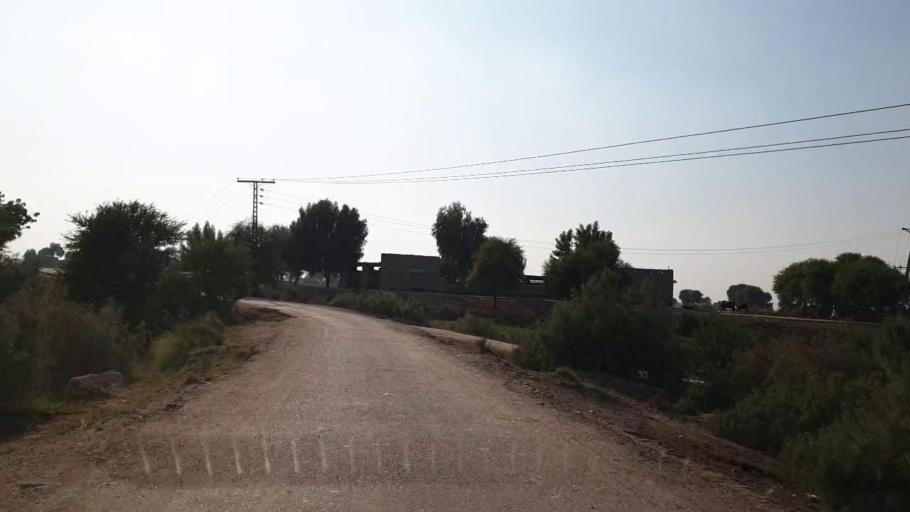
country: PK
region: Sindh
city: Sehwan
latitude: 26.4448
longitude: 67.8103
